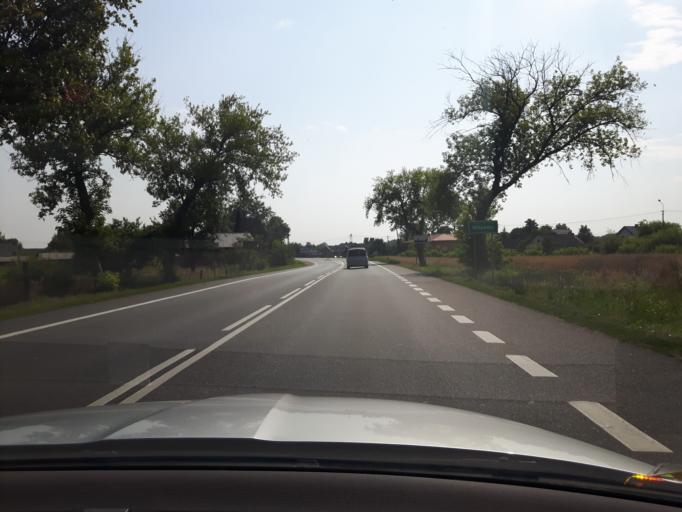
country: PL
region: Masovian Voivodeship
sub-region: Powiat mlawski
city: Strzegowo
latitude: 52.9446
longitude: 20.2834
